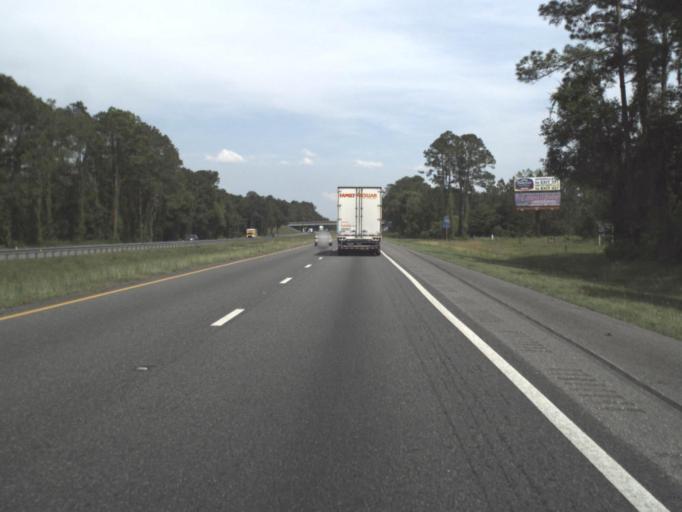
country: US
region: Florida
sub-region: Suwannee County
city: Wellborn
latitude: 30.2826
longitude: -82.8267
